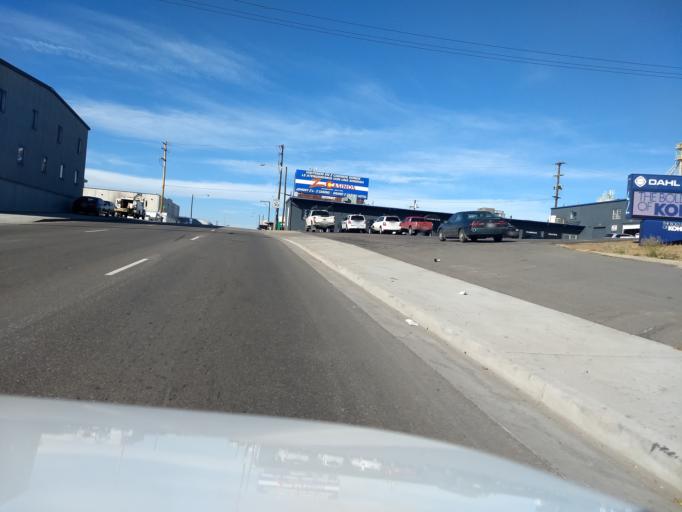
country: US
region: Colorado
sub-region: Denver County
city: Denver
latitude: 39.7116
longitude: -104.9973
